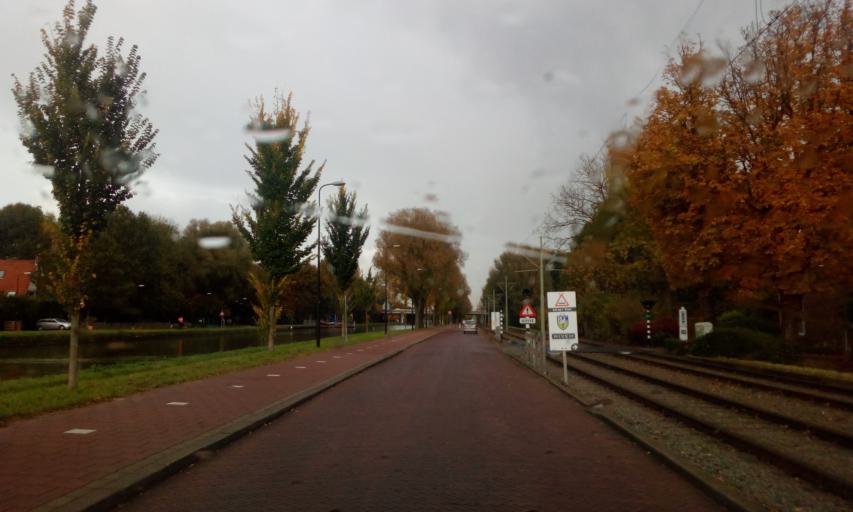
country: NL
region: South Holland
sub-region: Gemeente Rijswijk
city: Rijswijk
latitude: 52.0367
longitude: 4.3455
